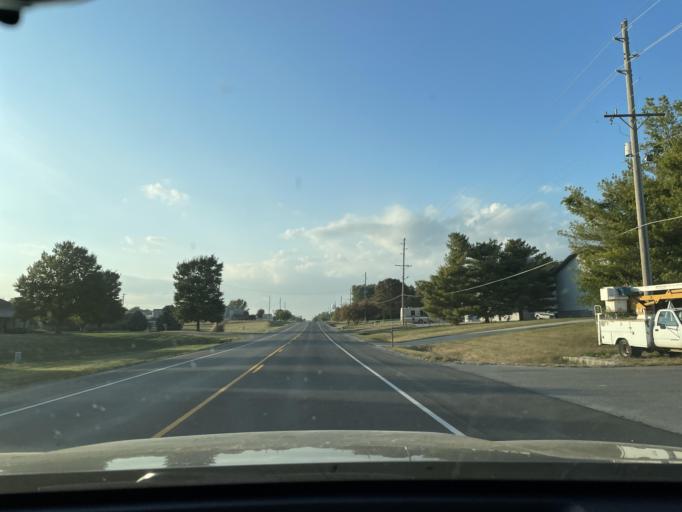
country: US
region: Missouri
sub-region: Andrew County
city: Country Club Village
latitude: 39.8214
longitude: -94.8490
